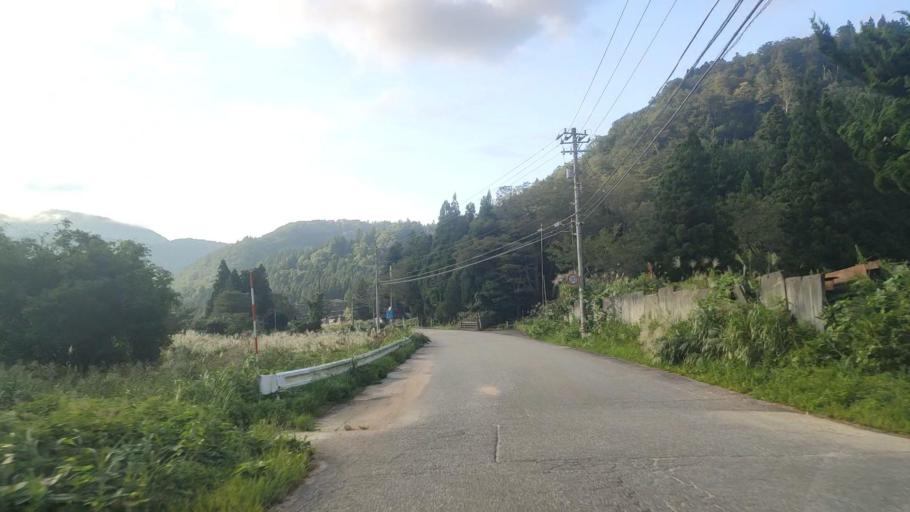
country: JP
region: Toyama
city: Yatsuomachi-higashikumisaka
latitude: 36.4775
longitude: 137.0840
